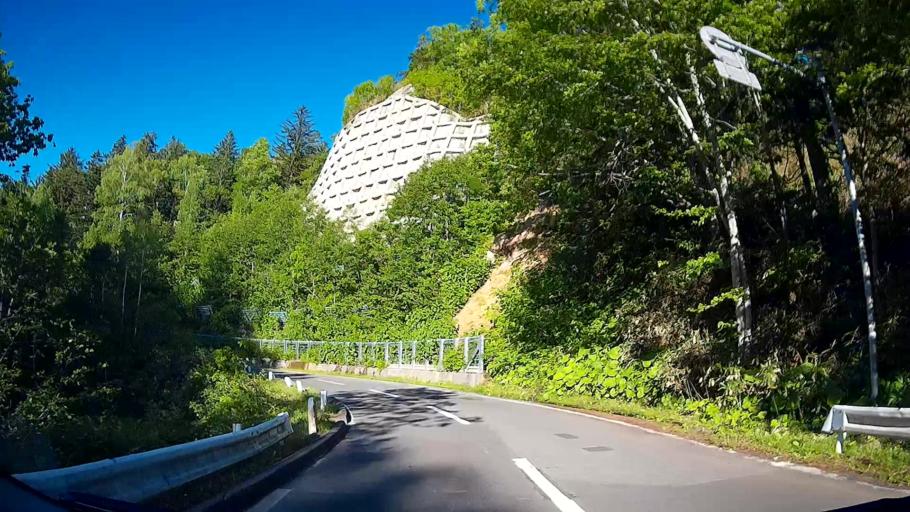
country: JP
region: Hokkaido
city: Otaru
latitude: 42.9859
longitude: 141.0695
